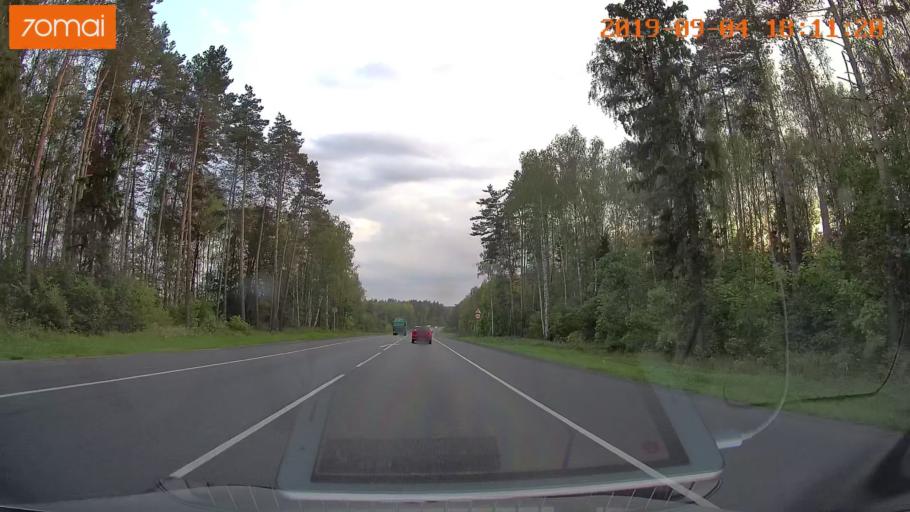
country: RU
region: Moskovskaya
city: Lopatinskiy
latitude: 55.3789
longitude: 38.7555
